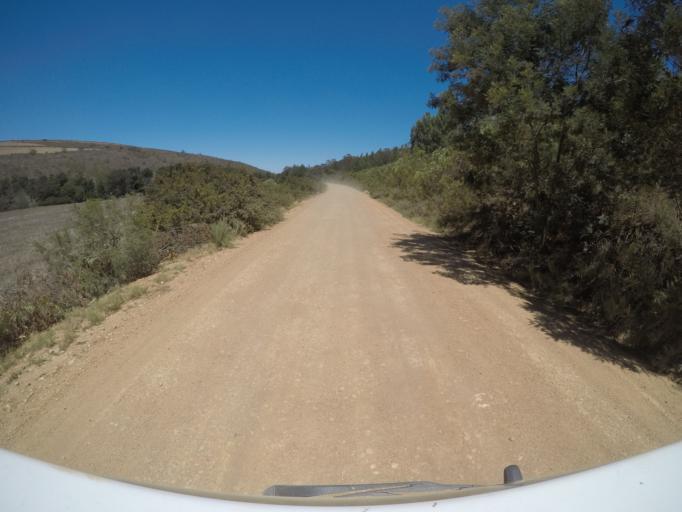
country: ZA
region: Western Cape
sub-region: Overberg District Municipality
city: Caledon
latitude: -34.1528
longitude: 19.2326
